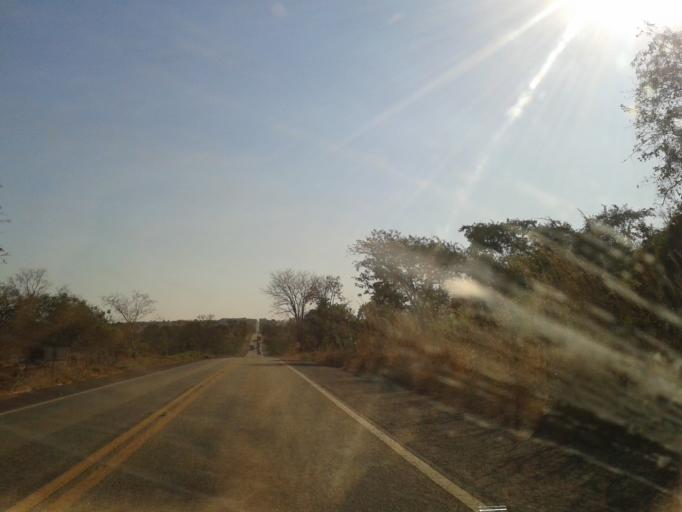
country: BR
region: Goias
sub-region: Mozarlandia
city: Mozarlandia
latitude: -15.0786
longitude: -50.6217
